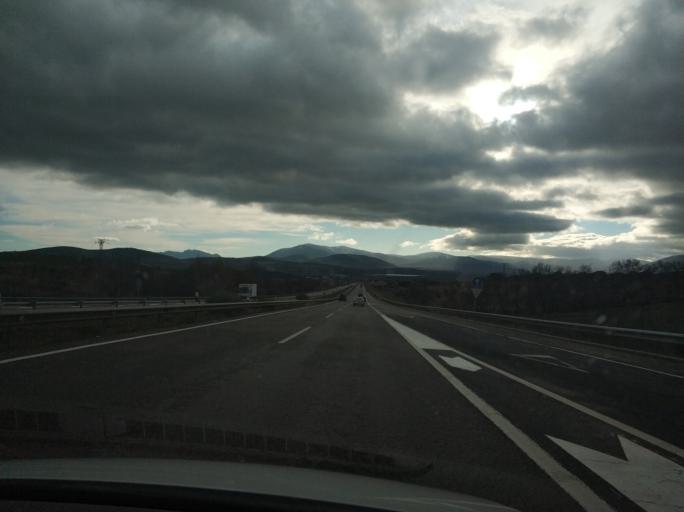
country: ES
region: Madrid
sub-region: Provincia de Madrid
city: Gascones
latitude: 41.0256
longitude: -3.6238
